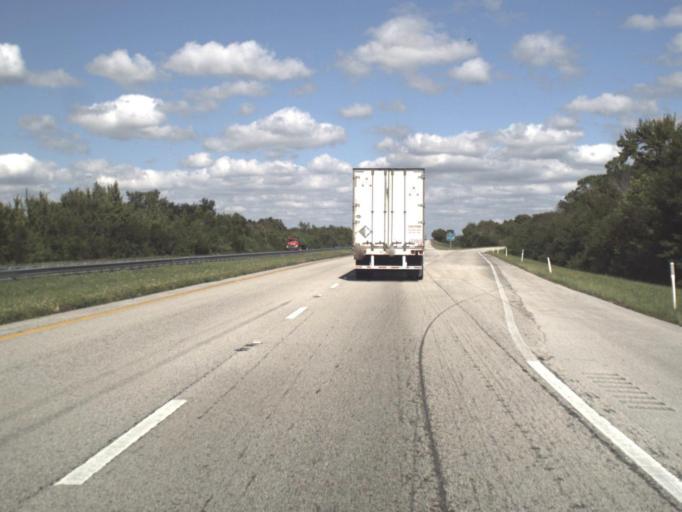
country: US
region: Florida
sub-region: Osceola County
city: Saint Cloud
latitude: 28.2577
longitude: -81.3315
